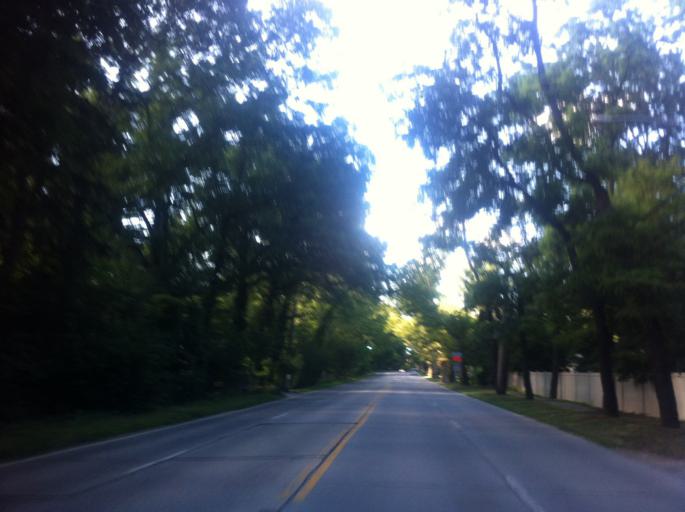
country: US
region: New York
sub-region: Nassau County
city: Lattingtown
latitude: 40.8980
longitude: -73.5825
